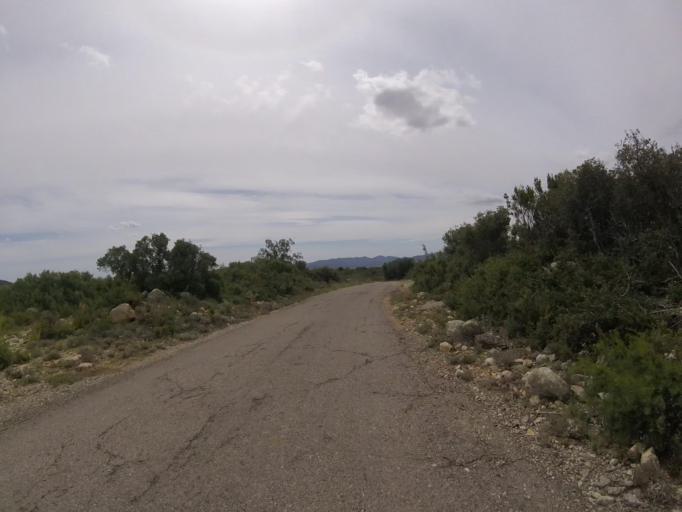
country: ES
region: Valencia
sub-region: Provincia de Castello
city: Sierra-Engarceran
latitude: 40.2462
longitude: -0.0282
